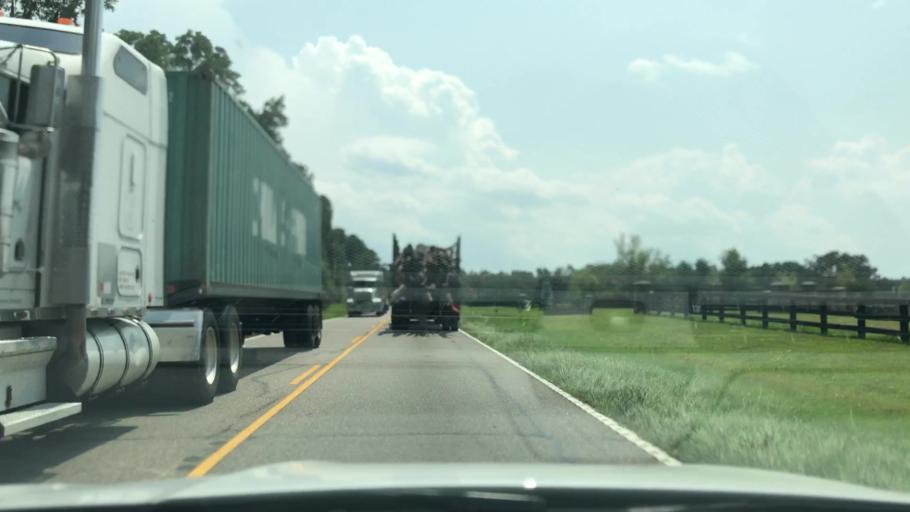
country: US
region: South Carolina
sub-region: Georgetown County
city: Georgetown
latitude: 33.4661
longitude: -79.2801
